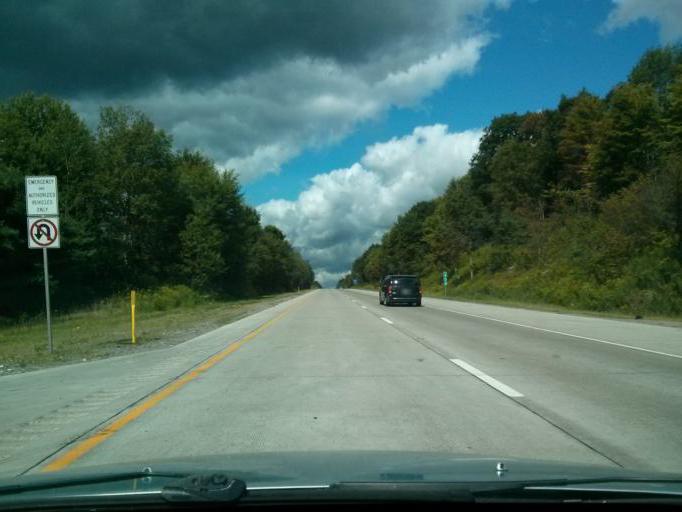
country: US
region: Pennsylvania
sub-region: Jefferson County
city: Falls Creek
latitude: 41.1527
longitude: -78.8055
